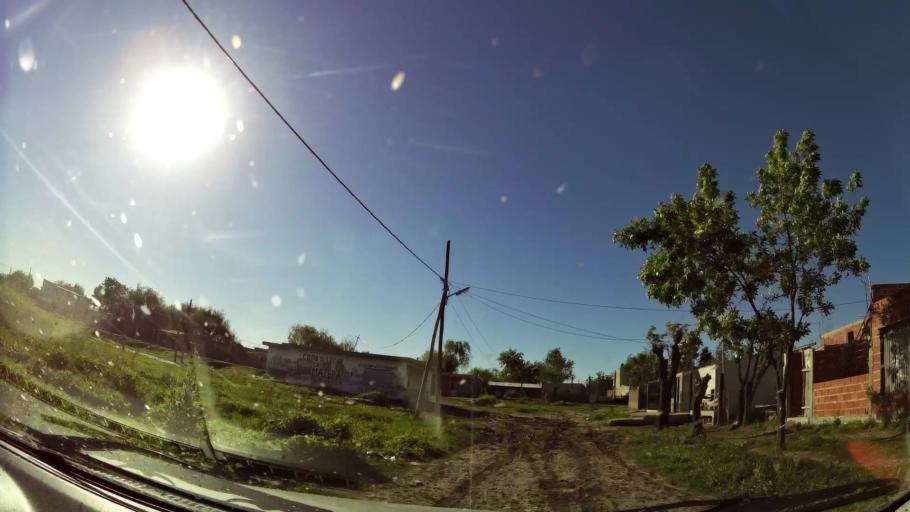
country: AR
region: Buenos Aires
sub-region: Partido de Quilmes
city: Quilmes
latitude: -34.7550
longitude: -58.3199
